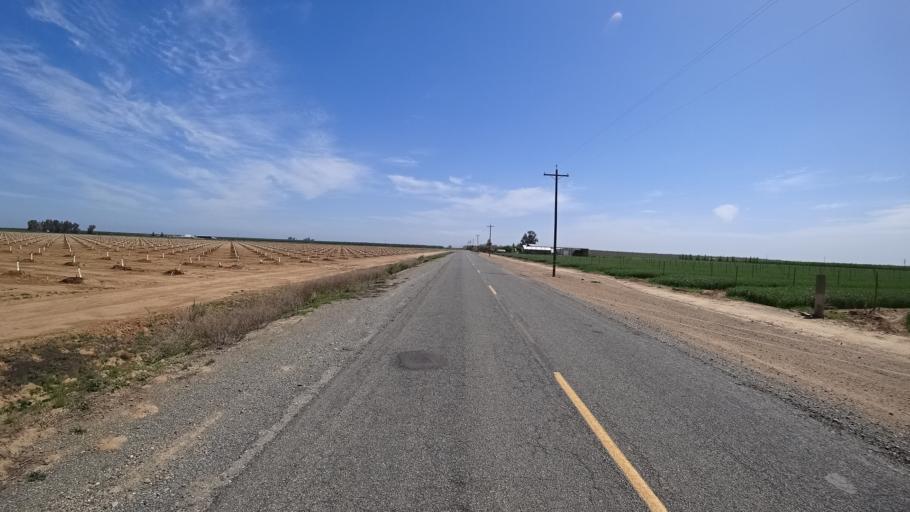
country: US
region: California
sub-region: Glenn County
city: Orland
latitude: 39.6527
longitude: -122.1107
